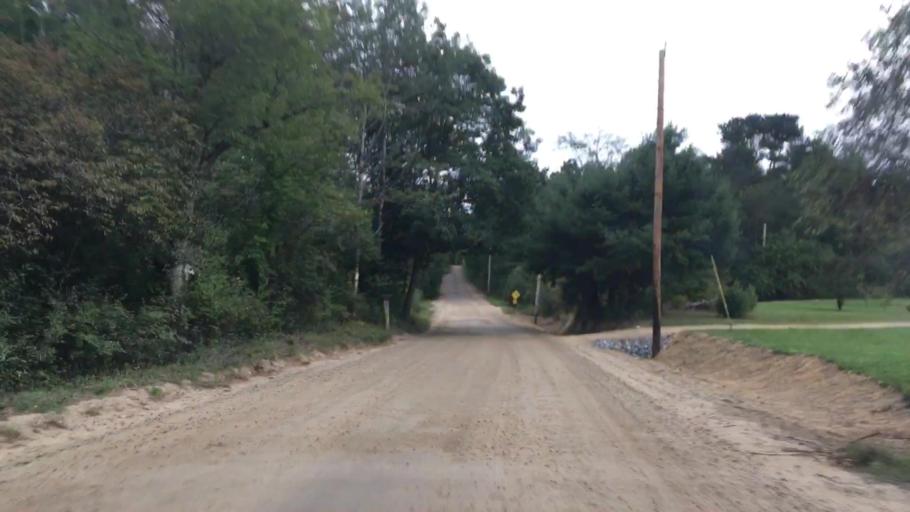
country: US
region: Maine
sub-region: Cumberland County
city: New Gloucester
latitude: 43.9075
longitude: -70.2369
